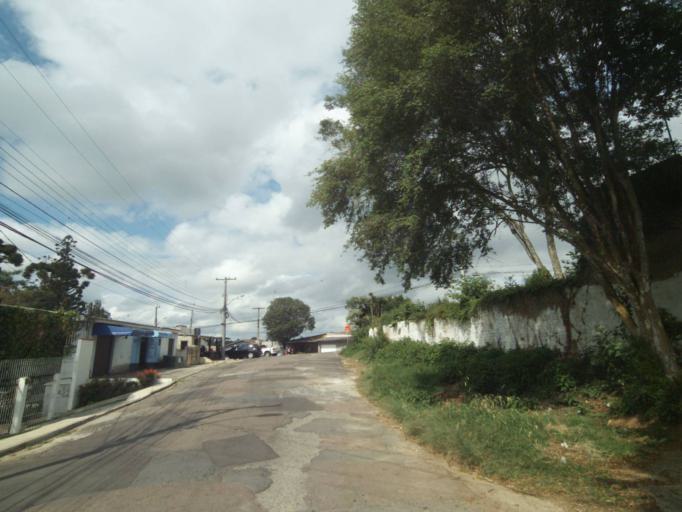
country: BR
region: Parana
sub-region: Curitiba
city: Curitiba
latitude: -25.3793
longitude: -49.2930
